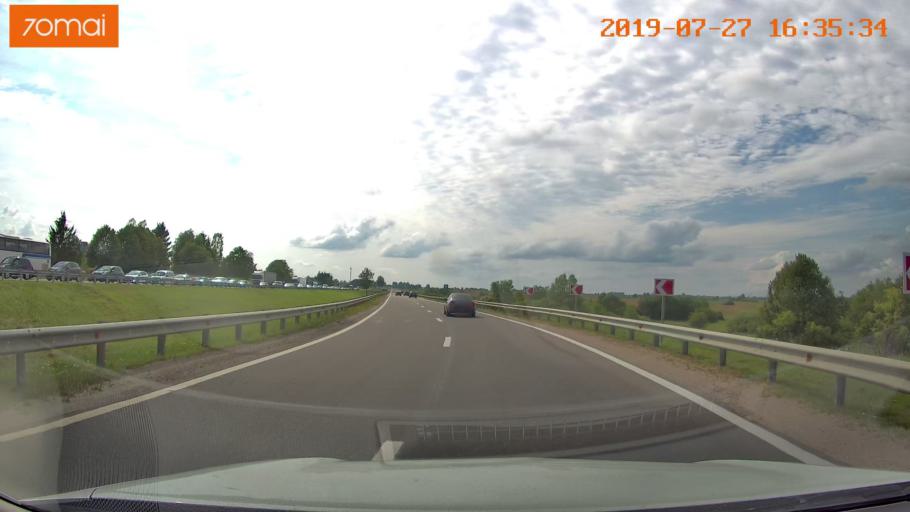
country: RU
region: Kaliningrad
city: Gvardeysk
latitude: 54.6493
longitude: 21.3060
